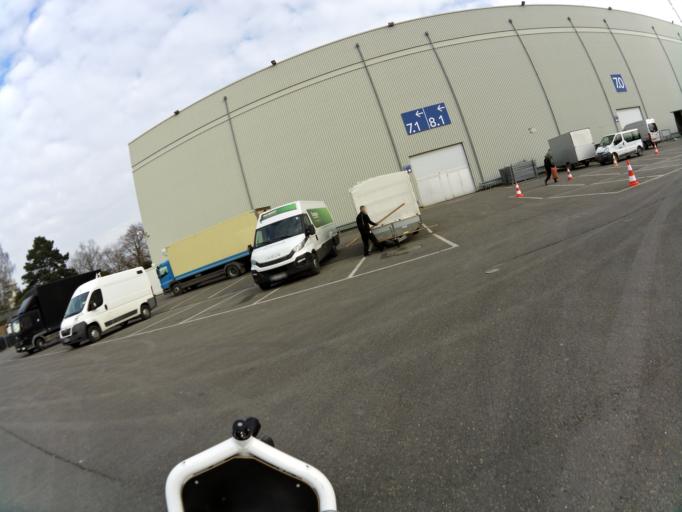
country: DE
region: North Rhine-Westphalia
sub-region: Regierungsbezirk Dusseldorf
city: Essen
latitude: 51.4292
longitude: 6.9920
